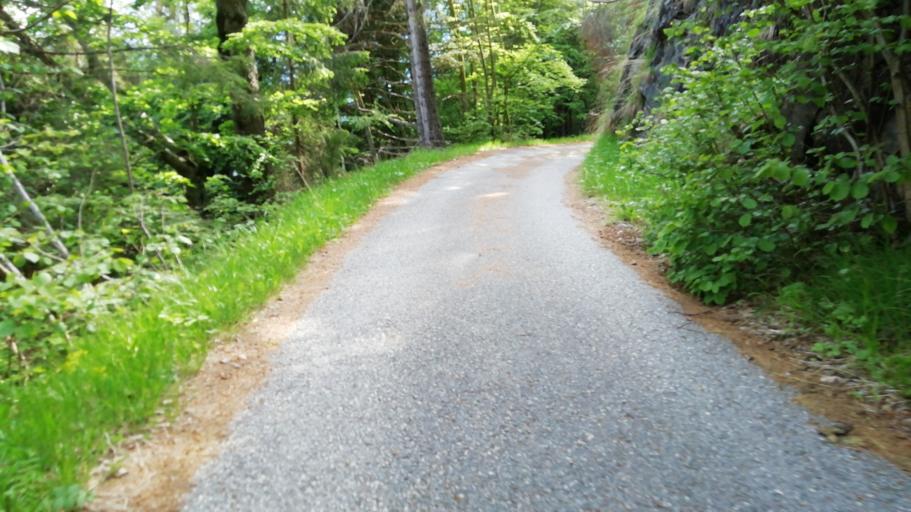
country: IT
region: Veneto
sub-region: Provincia di Belluno
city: Valle di Cadore
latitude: 46.4253
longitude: 12.3204
